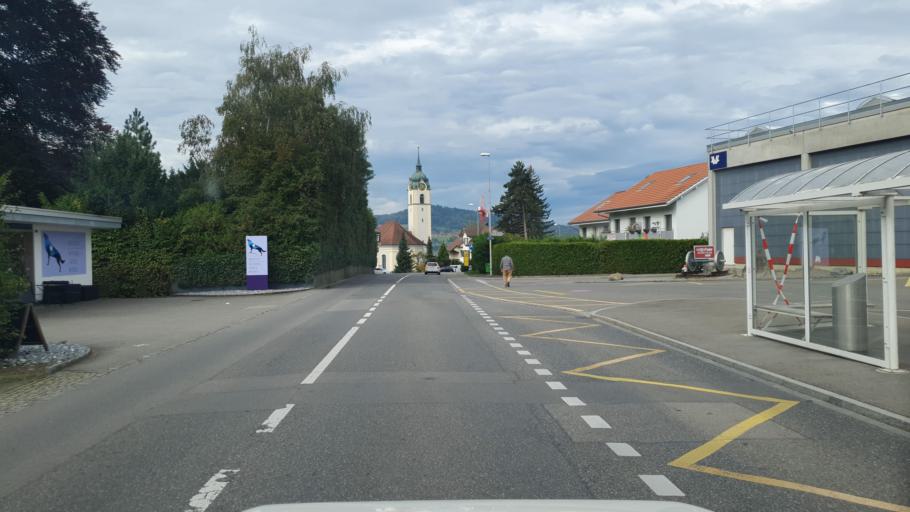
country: CH
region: Aargau
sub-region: Bezirk Lenzburg
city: Meisterschwanden
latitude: 47.2951
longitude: 8.2376
